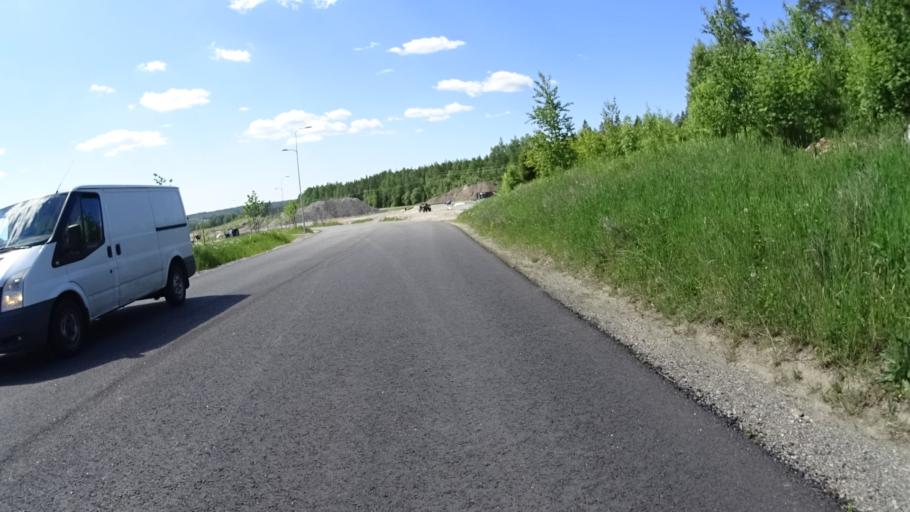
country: FI
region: Uusimaa
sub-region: Helsinki
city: Nurmijaervi
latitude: 60.4439
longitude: 24.8359
